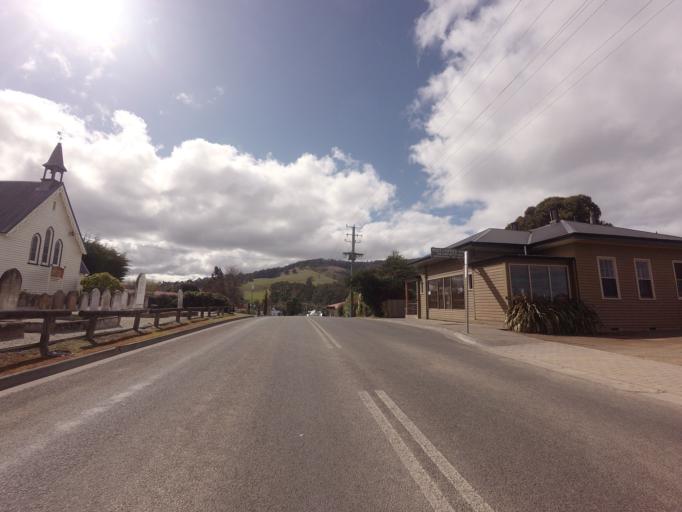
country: AU
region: Tasmania
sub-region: Huon Valley
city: Cygnet
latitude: -43.3138
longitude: 147.0152
